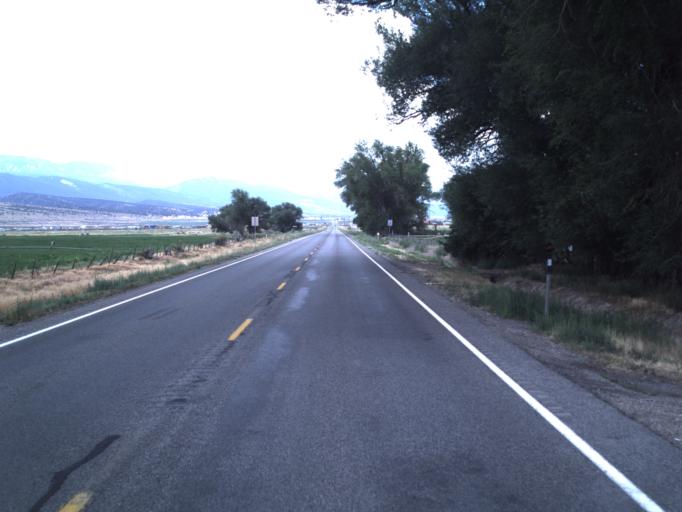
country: US
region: Utah
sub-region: Sanpete County
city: Moroni
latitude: 39.4726
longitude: -111.5629
